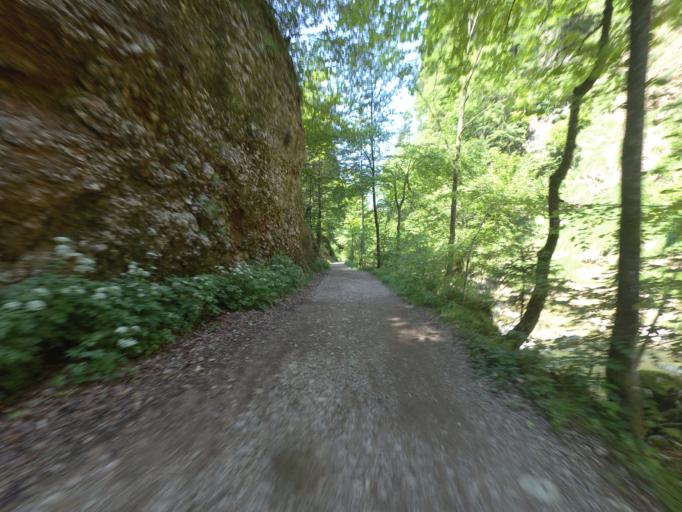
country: AT
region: Salzburg
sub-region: Politischer Bezirk Salzburg-Umgebung
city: Elsbethen
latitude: 47.7677
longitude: 13.0989
